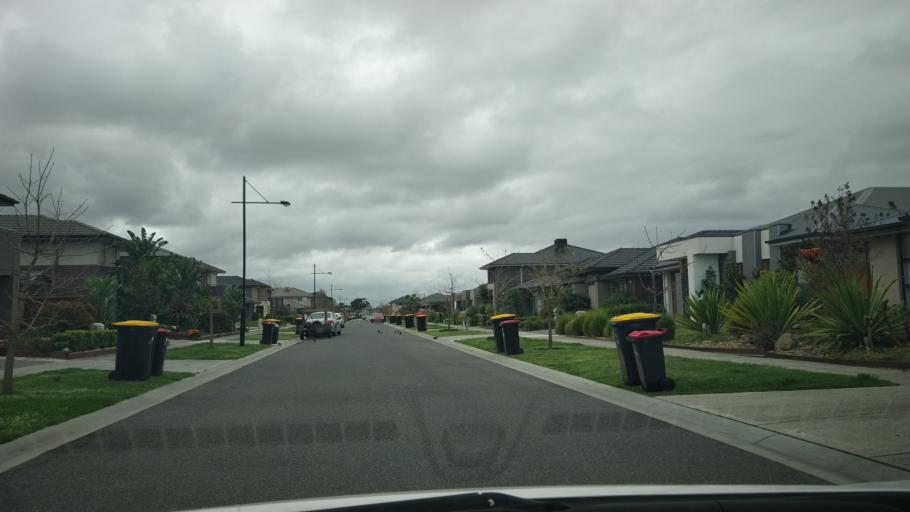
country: AU
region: Victoria
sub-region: Greater Dandenong
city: Keysborough
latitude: -38.0095
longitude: 145.1775
